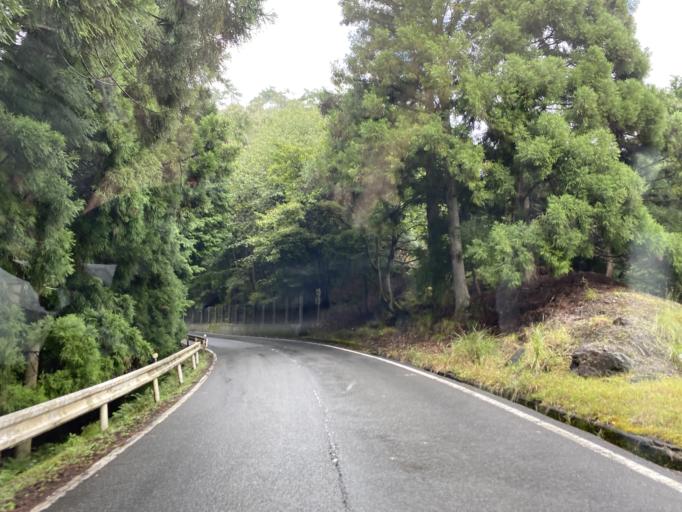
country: JP
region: Kyoto
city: Fukuchiyama
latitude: 35.3024
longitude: 134.9513
